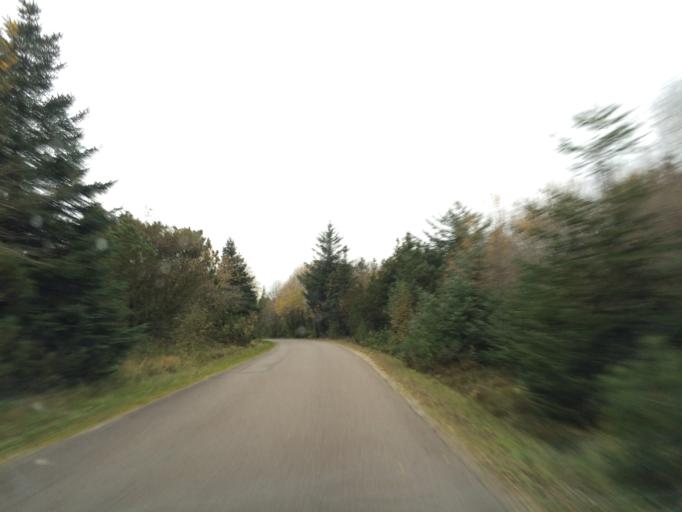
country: DK
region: Central Jutland
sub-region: Holstebro Kommune
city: Ulfborg
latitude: 56.2376
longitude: 8.4198
